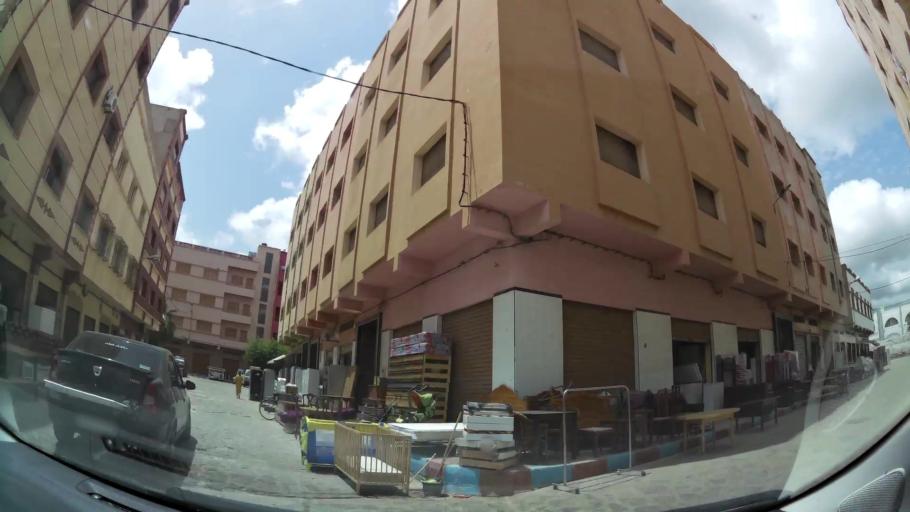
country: MA
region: Oriental
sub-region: Nador
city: Nador
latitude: 35.1741
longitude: -2.9198
